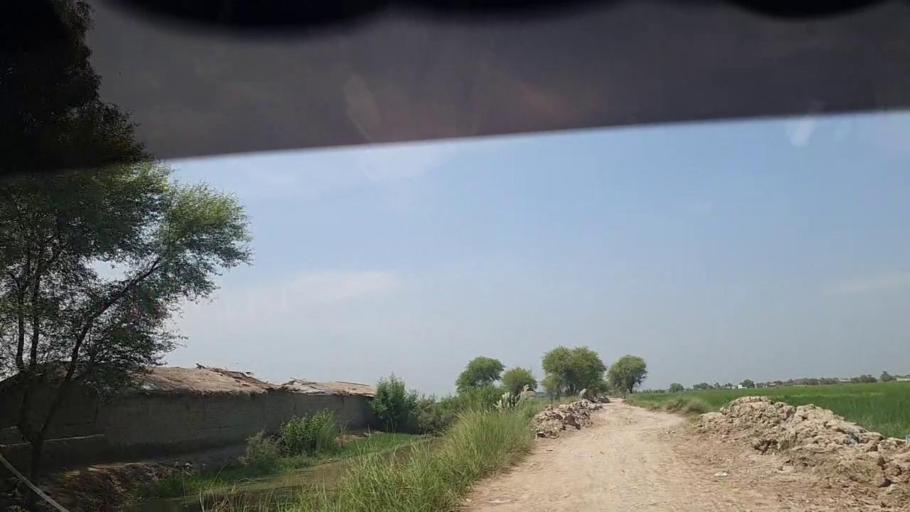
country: PK
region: Sindh
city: Thul
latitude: 28.1845
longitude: 68.7216
